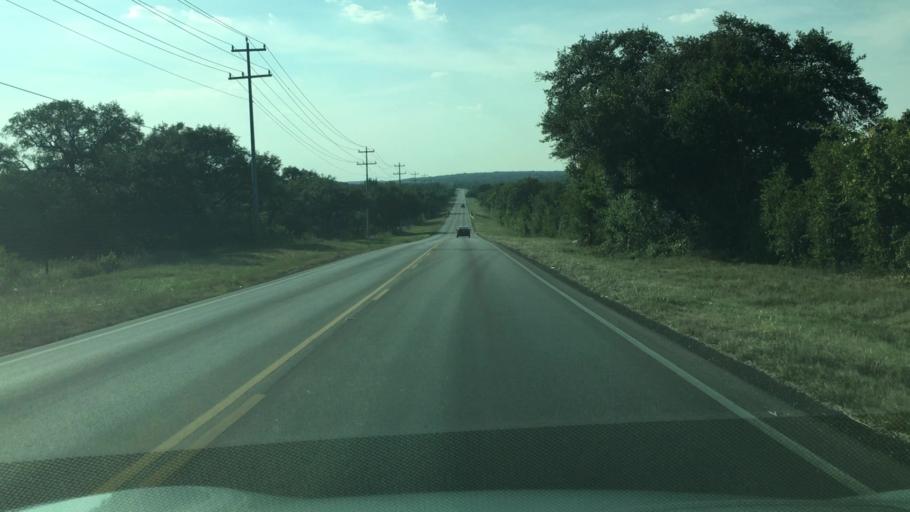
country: US
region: Texas
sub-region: Travis County
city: Shady Hollow
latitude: 30.1040
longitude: -97.9405
